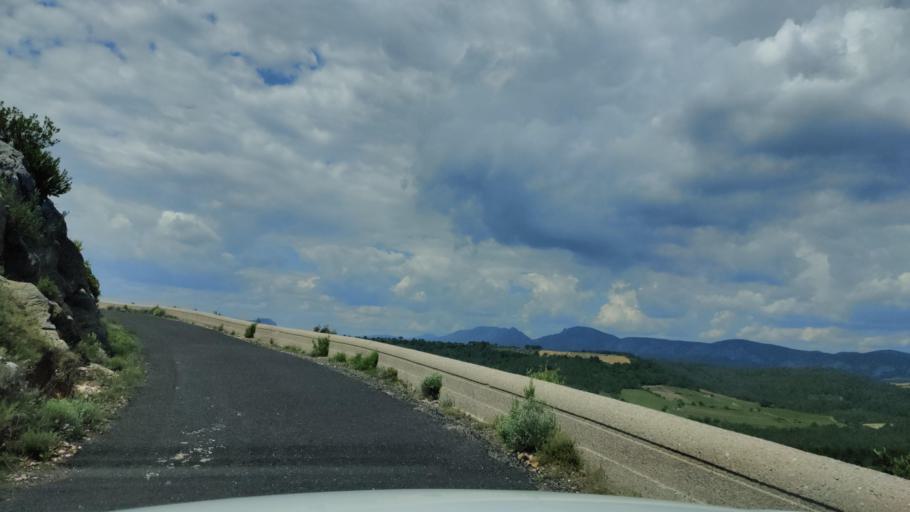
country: FR
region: Languedoc-Roussillon
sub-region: Departement des Pyrenees-Orientales
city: Estagel
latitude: 42.7992
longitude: 2.7246
